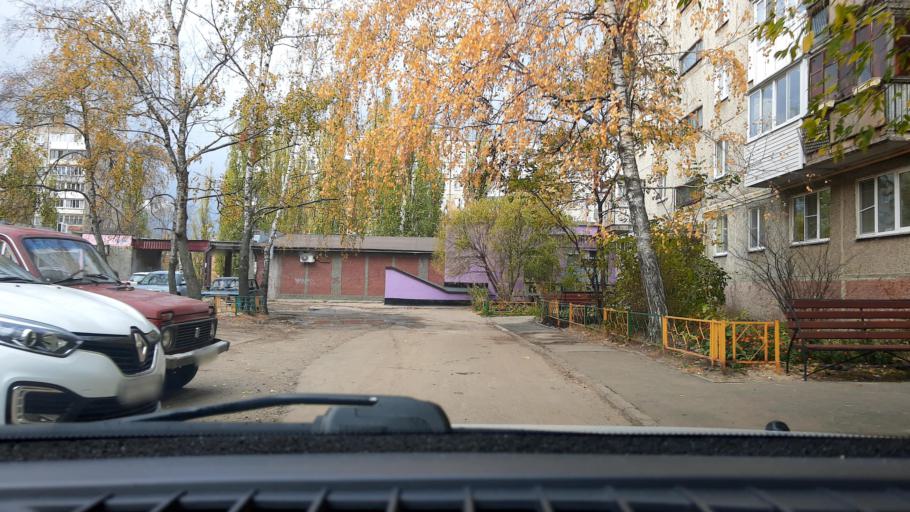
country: RU
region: Nizjnij Novgorod
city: Gorbatovka
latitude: 56.3652
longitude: 43.8229
